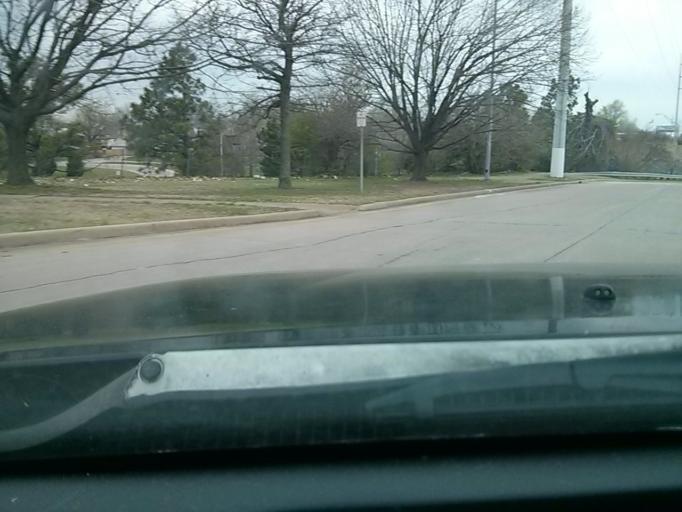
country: US
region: Oklahoma
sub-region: Tulsa County
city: Tulsa
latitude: 36.1450
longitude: -95.9924
